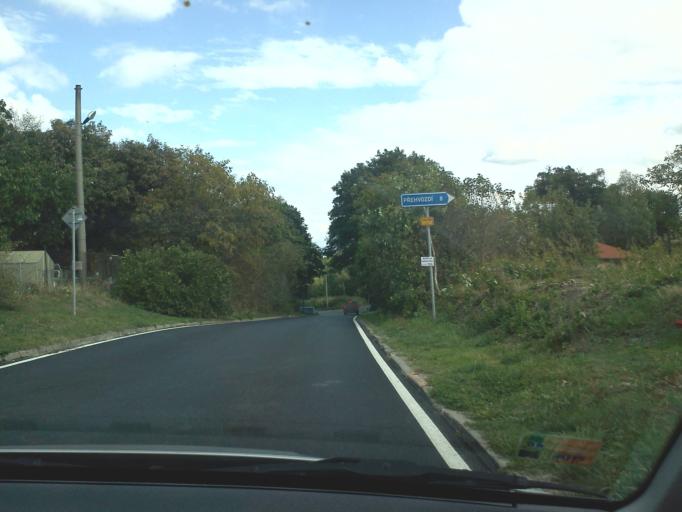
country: CZ
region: Central Bohemia
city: Mukarov
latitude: 50.0231
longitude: 14.7963
